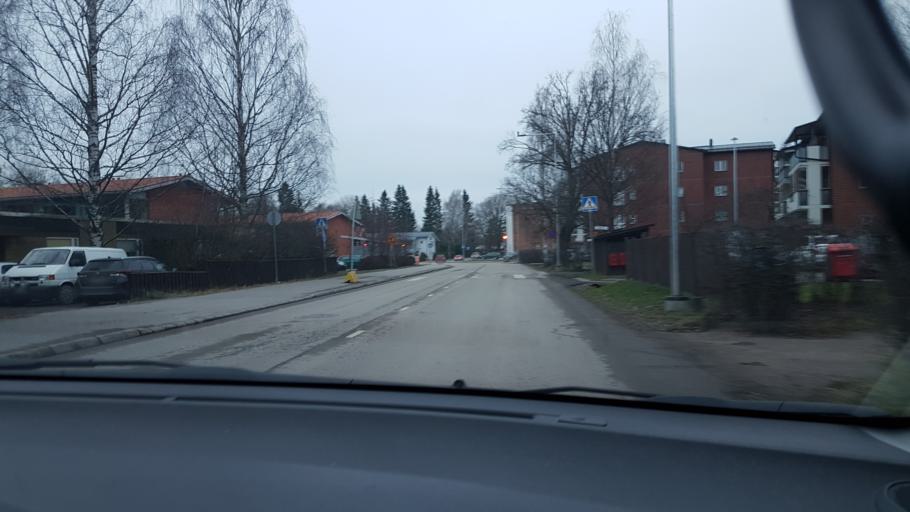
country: FI
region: Uusimaa
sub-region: Helsinki
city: Vantaa
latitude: 60.2930
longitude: 25.0169
